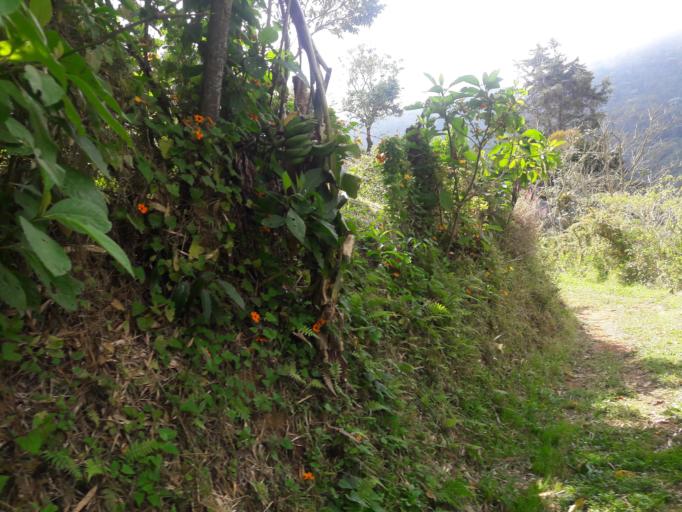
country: CO
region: Valle del Cauca
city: Cali
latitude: 3.4574
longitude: -76.6589
